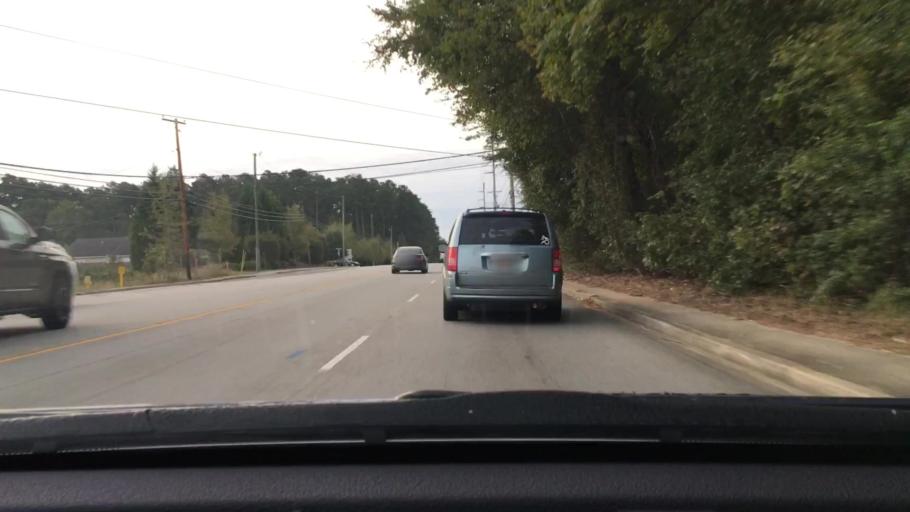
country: US
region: South Carolina
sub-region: Lexington County
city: Saint Andrews
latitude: 34.0642
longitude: -81.1157
